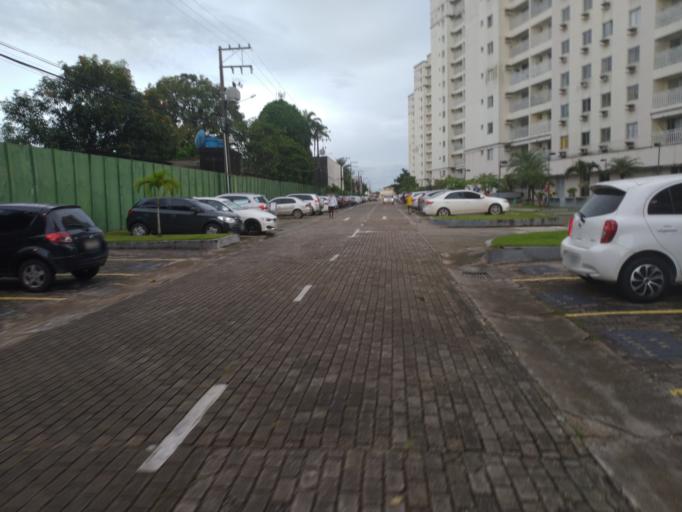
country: BR
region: Para
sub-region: Ananindeua
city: Ananindeua
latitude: -1.3644
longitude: -48.3765
